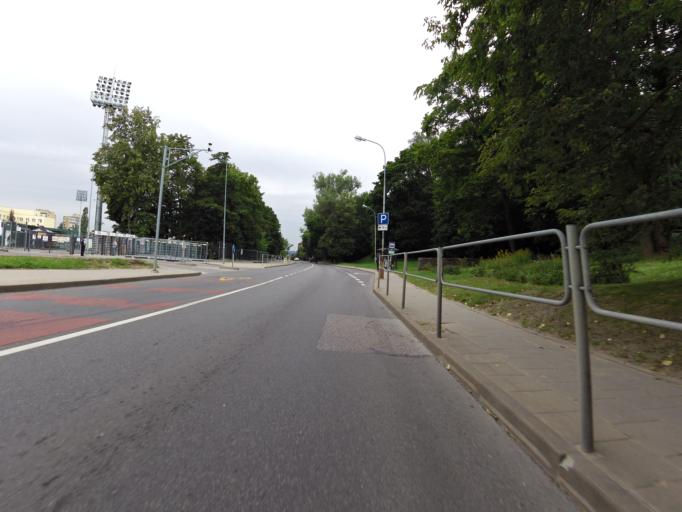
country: LT
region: Vilnius County
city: Rasos
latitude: 54.6681
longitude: 25.2967
